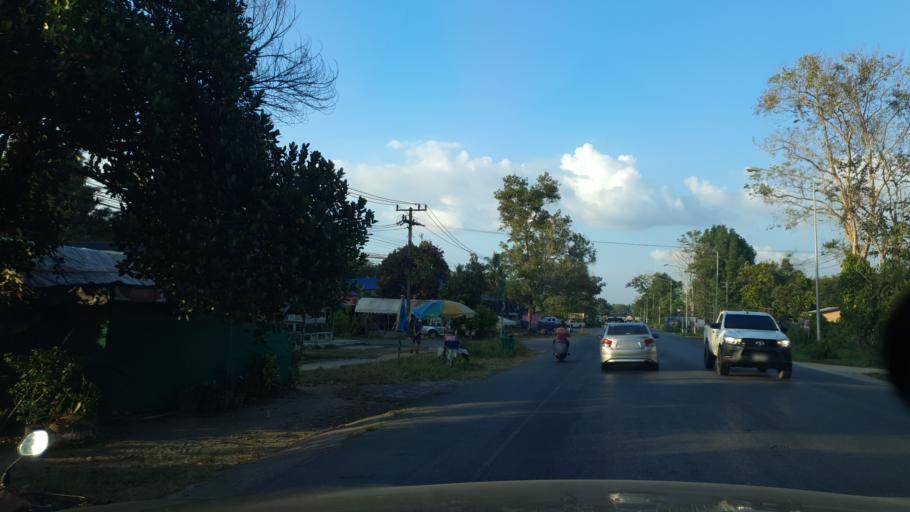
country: TH
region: Phangnga
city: Takua Pa
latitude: 8.8341
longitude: 98.2835
